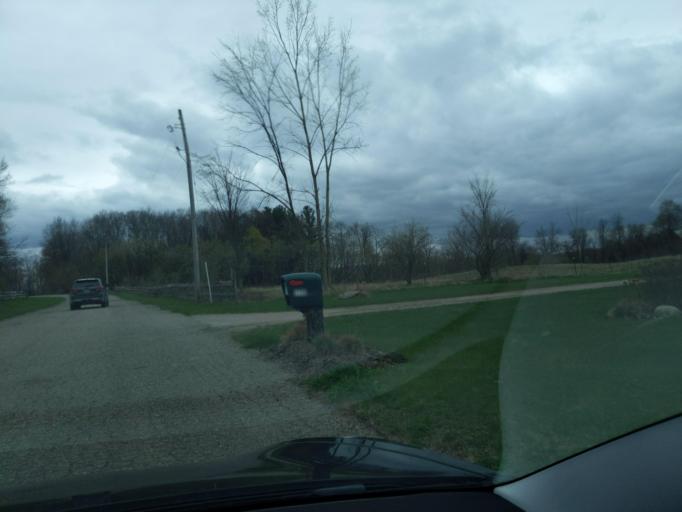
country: US
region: Michigan
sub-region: Ingham County
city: Stockbridge
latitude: 42.4550
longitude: -84.0916
